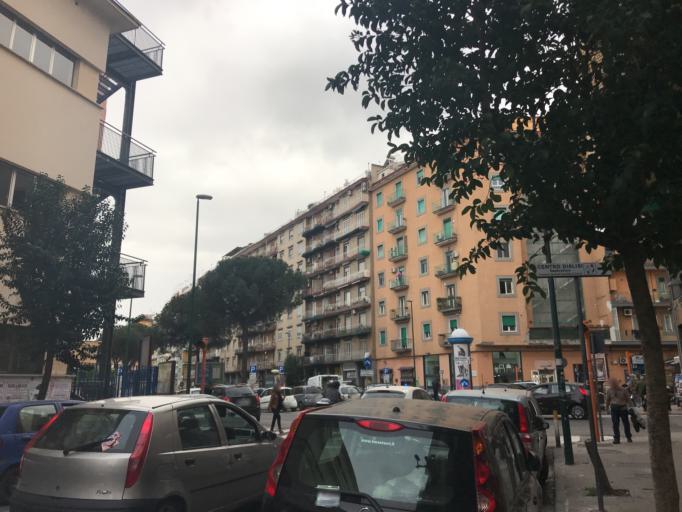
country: IT
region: Campania
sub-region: Provincia di Napoli
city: Napoli
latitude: 40.8511
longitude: 14.2275
